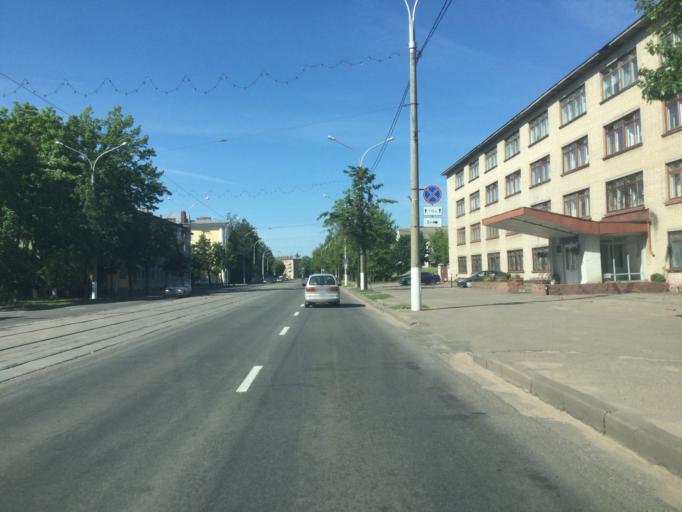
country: BY
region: Vitebsk
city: Vitebsk
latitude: 55.1871
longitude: 30.1891
